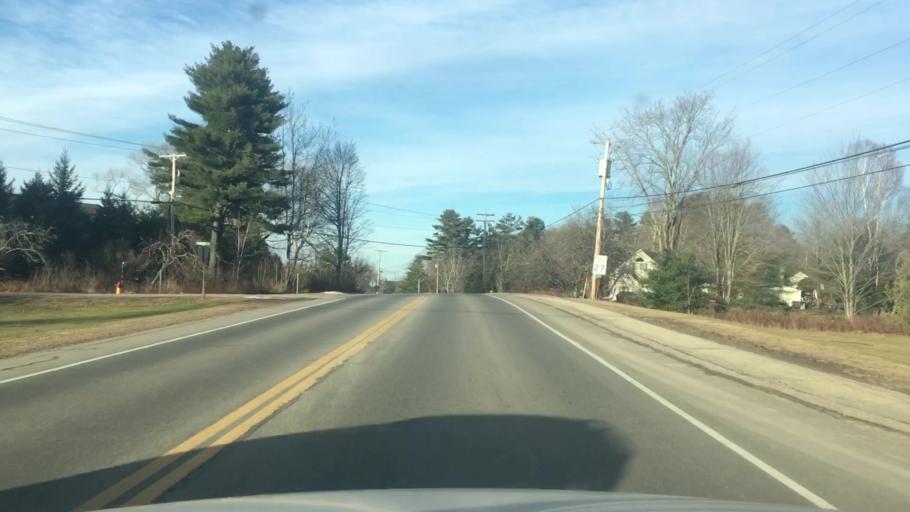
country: US
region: Maine
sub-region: Lincoln County
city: Wiscasset
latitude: 44.0103
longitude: -69.6680
